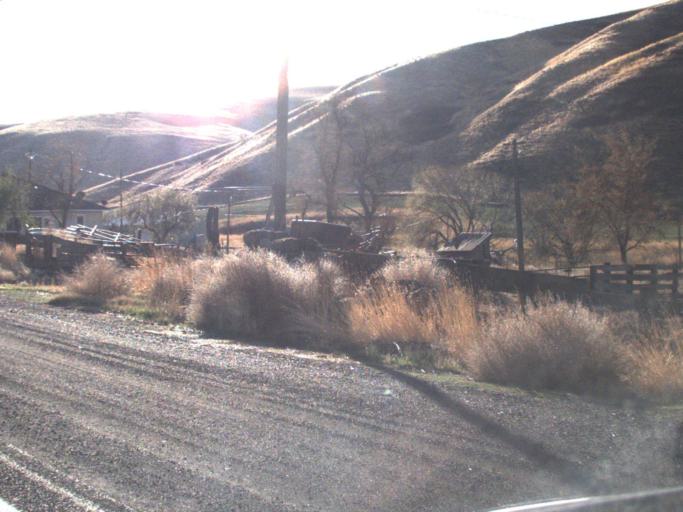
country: US
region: Washington
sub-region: Garfield County
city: Pomeroy
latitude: 46.4896
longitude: -117.7620
